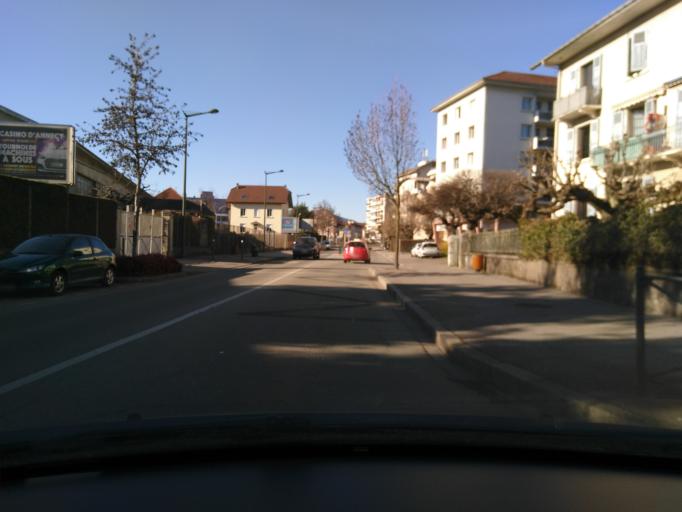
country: FR
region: Rhone-Alpes
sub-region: Departement de la Haute-Savoie
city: Annecy
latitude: 45.9045
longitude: 6.1156
